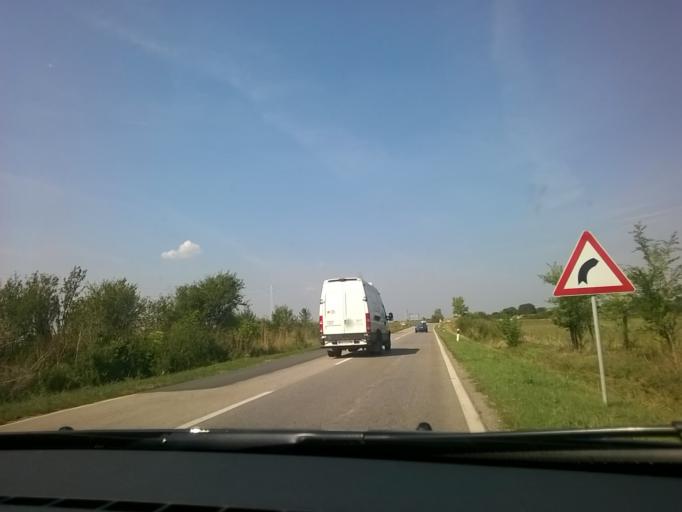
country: RS
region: Autonomna Pokrajina Vojvodina
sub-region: Juznobanatski Okrug
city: Vrsac
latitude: 45.1270
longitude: 21.2740
